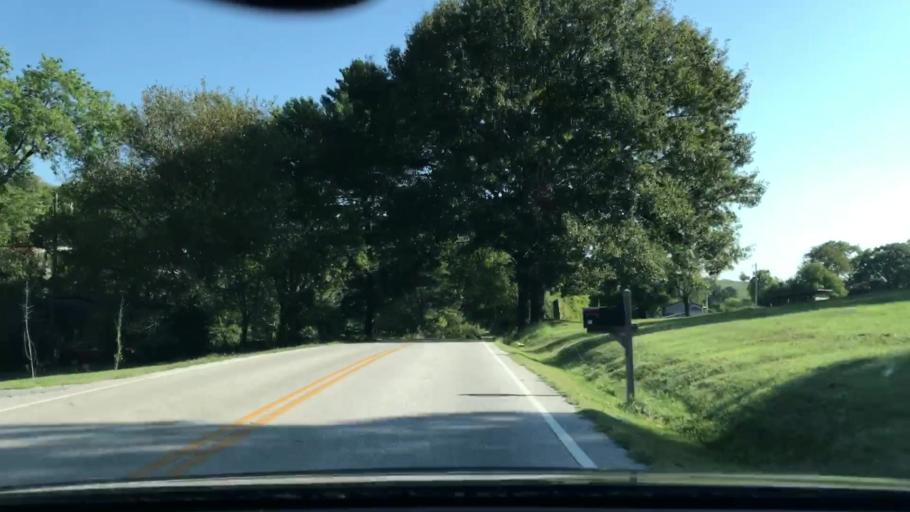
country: US
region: Tennessee
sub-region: Smith County
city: Carthage
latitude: 36.2755
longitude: -85.9521
